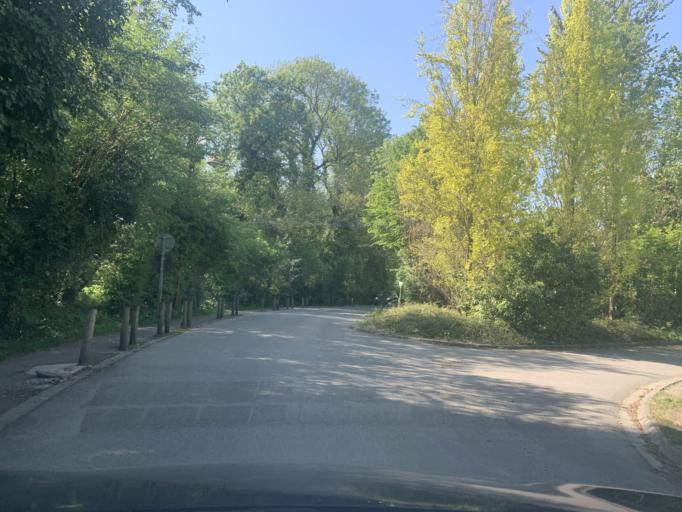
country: FR
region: Nord-Pas-de-Calais
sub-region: Departement du Nord
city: Proville
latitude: 50.1645
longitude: 3.2083
